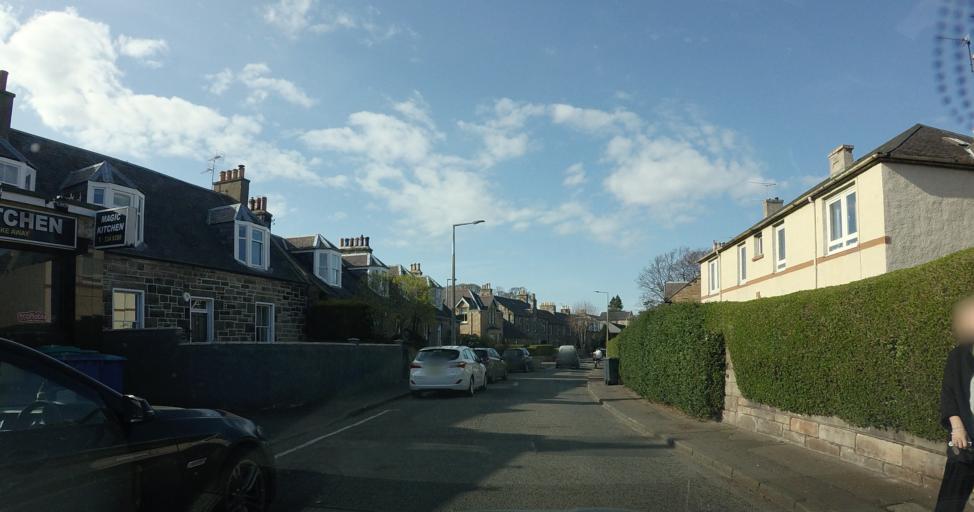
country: GB
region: Scotland
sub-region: Edinburgh
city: Colinton
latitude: 55.9411
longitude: -3.2841
